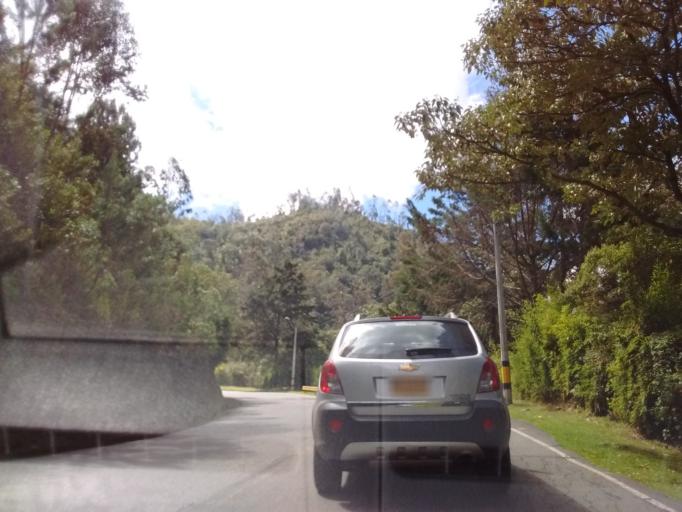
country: CO
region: Antioquia
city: Medellin
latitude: 6.2328
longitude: -75.5073
